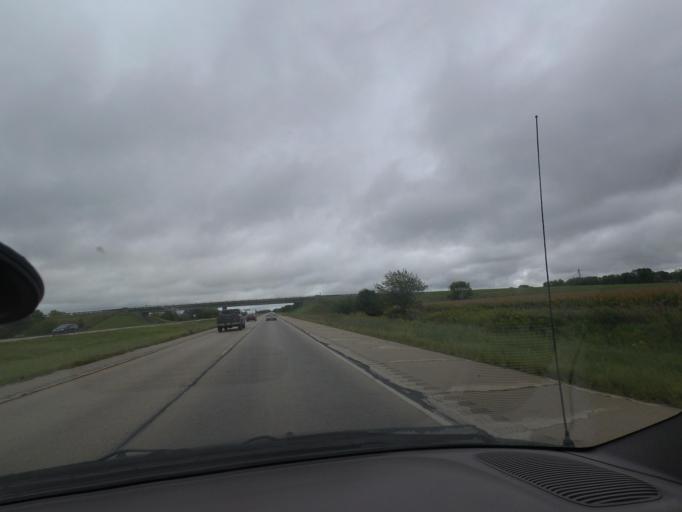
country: US
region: Illinois
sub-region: Piatt County
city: Cerro Gordo
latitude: 40.0179
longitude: -88.7278
